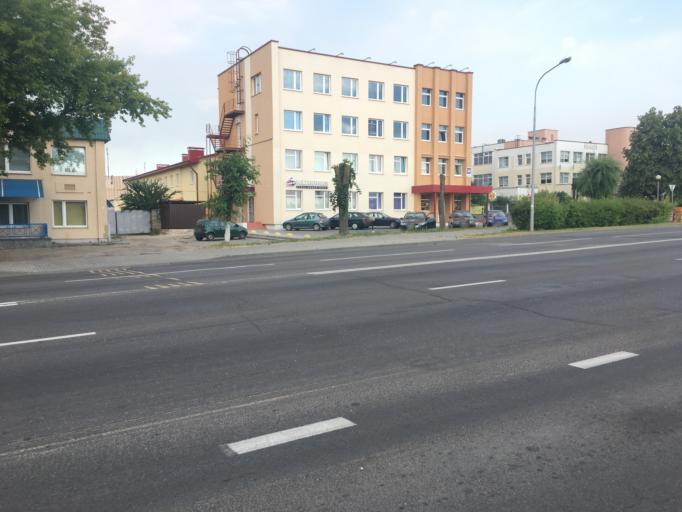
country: BY
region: Grodnenskaya
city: Hrodna
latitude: 53.6546
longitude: 23.8308
